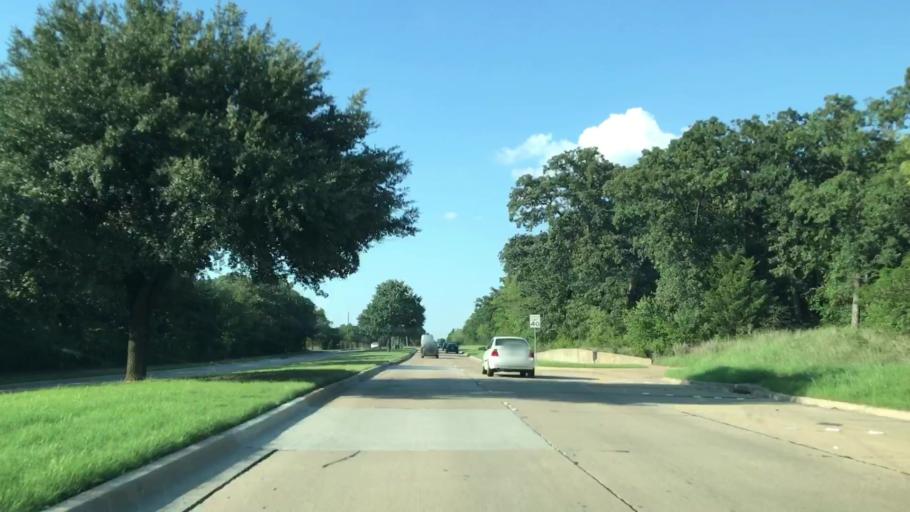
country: US
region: Texas
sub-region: Dallas County
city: Coppell
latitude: 32.9988
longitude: -97.0065
